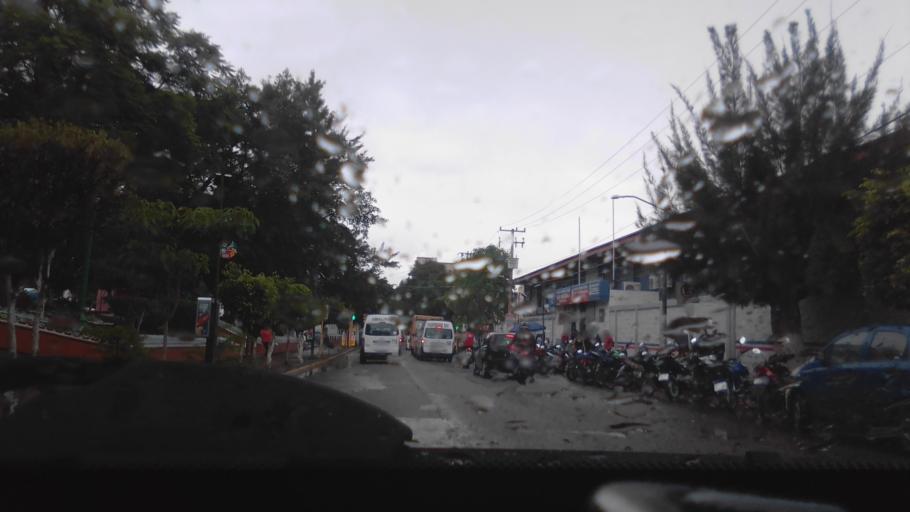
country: MX
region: Guerrero
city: Chilpancingo de los Bravos
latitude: 17.5559
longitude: -99.5044
